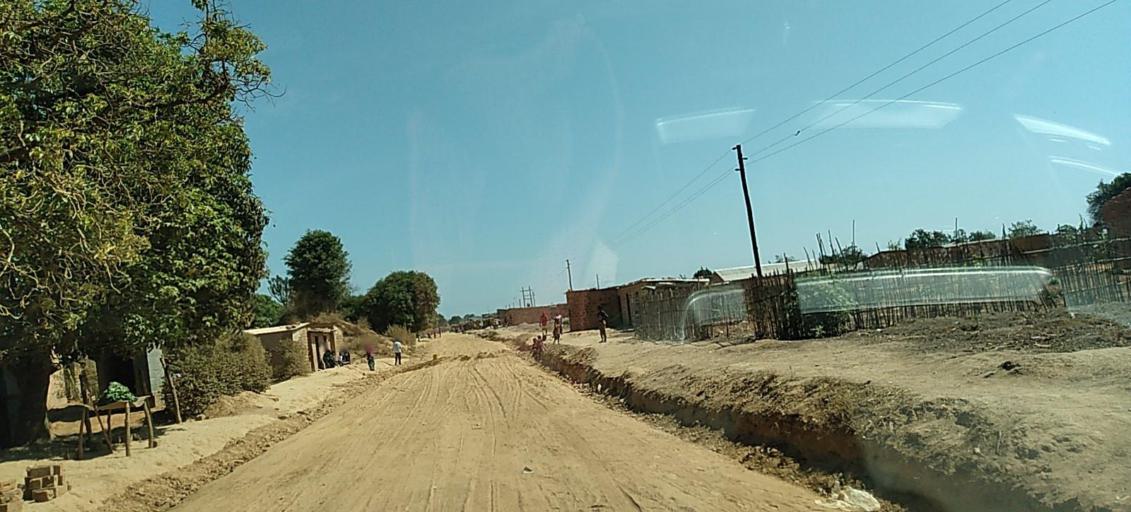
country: ZM
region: Copperbelt
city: Chililabombwe
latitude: -12.3297
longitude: 27.8602
